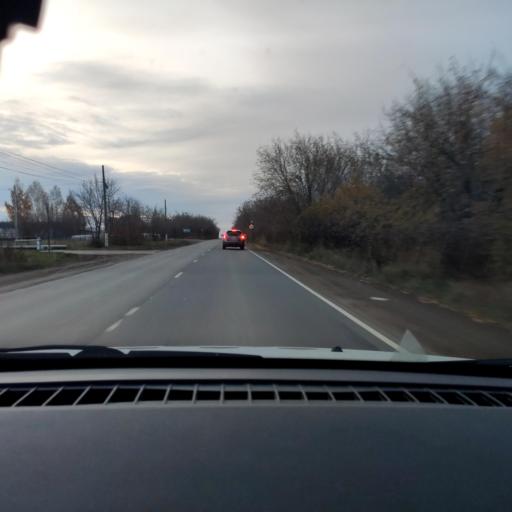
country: RU
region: Perm
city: Gamovo
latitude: 57.9060
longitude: 56.1684
